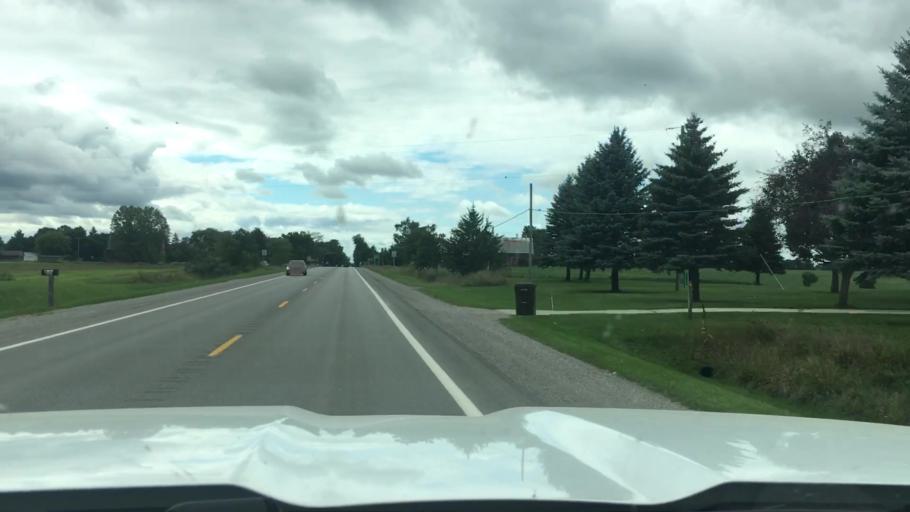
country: US
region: Michigan
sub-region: Montcalm County
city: Carson City
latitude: 43.1765
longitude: -84.8317
